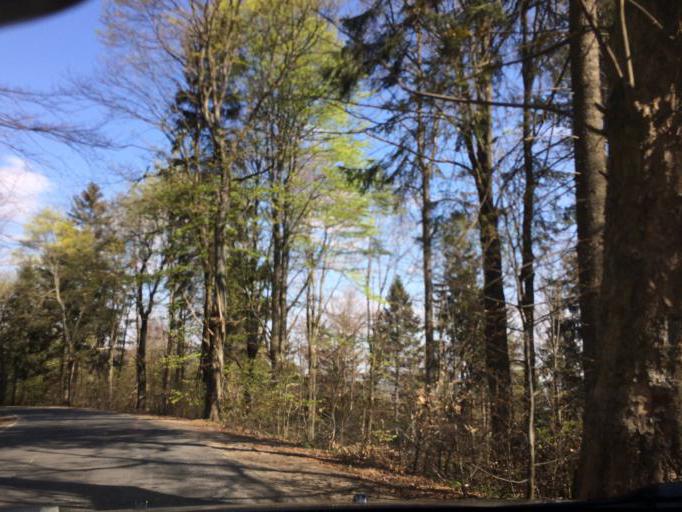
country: PL
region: Lower Silesian Voivodeship
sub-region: Powiat klodzki
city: Jugow
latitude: 50.6570
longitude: 16.5264
